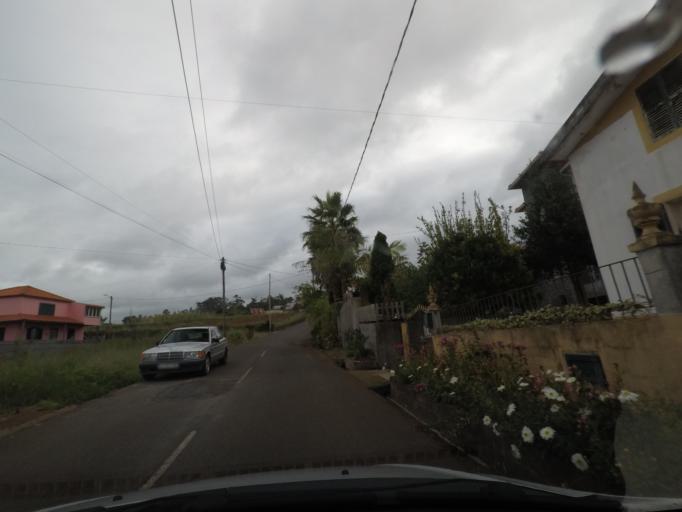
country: PT
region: Madeira
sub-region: Santana
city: Santana
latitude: 32.7897
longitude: -16.8732
